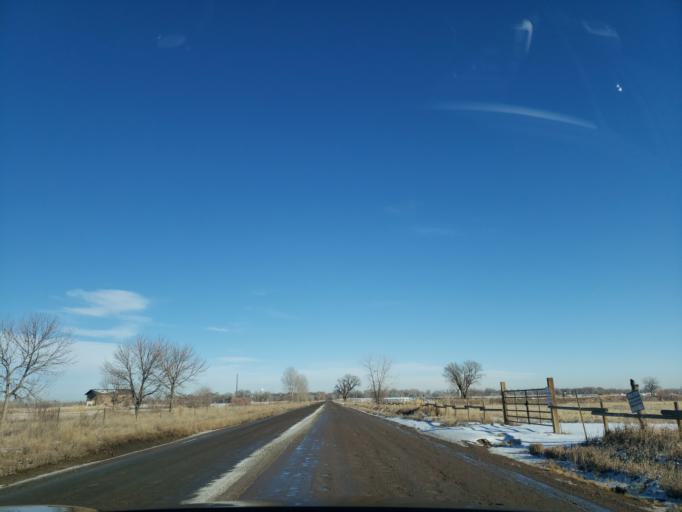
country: US
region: Colorado
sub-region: Larimer County
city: Fort Collins
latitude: 40.5377
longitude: -105.0118
